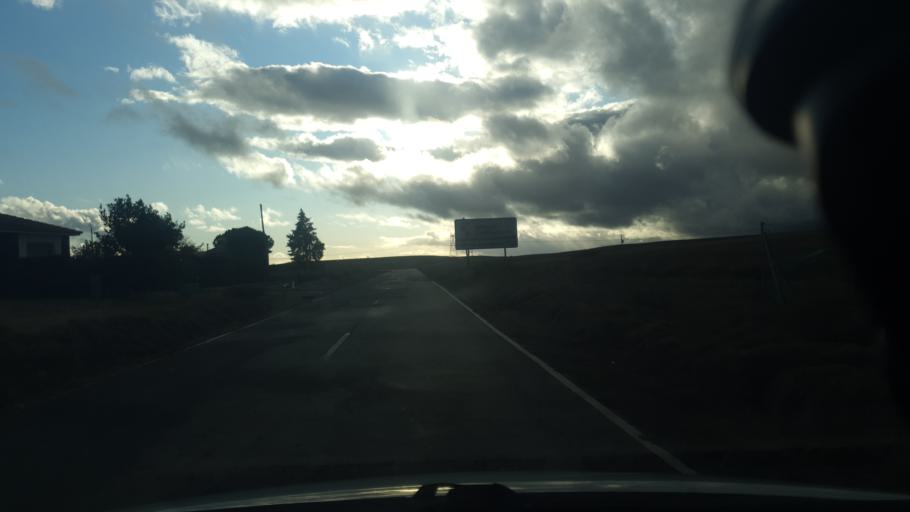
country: ES
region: Castille and Leon
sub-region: Provincia de Segovia
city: Santiuste de San Juan Bautista
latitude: 41.1528
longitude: -4.5746
